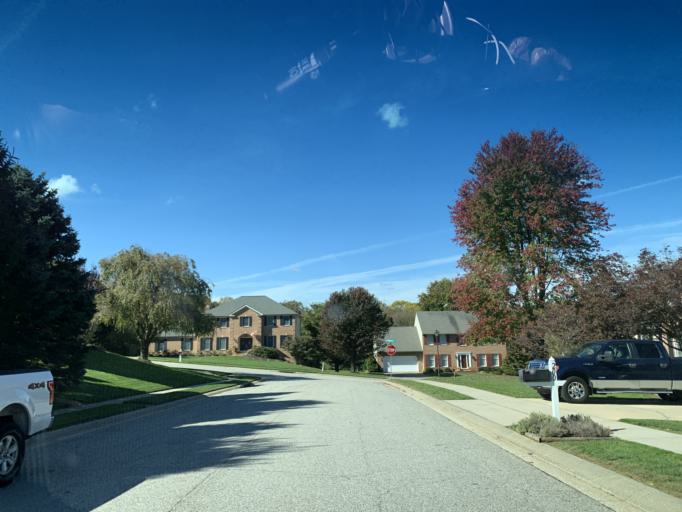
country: US
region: Maryland
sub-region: Harford County
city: Bel Air South
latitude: 39.5137
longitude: -76.3172
